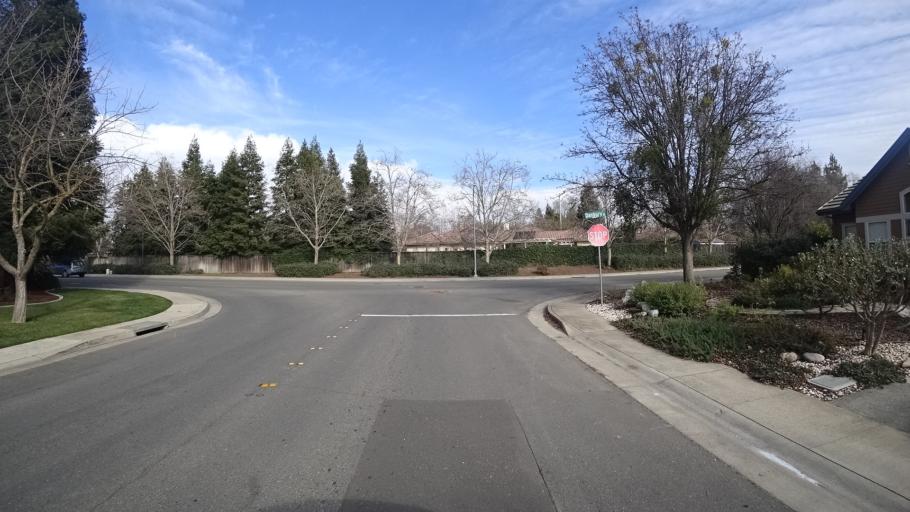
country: US
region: California
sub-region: Yolo County
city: Davis
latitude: 38.5407
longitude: -121.7148
